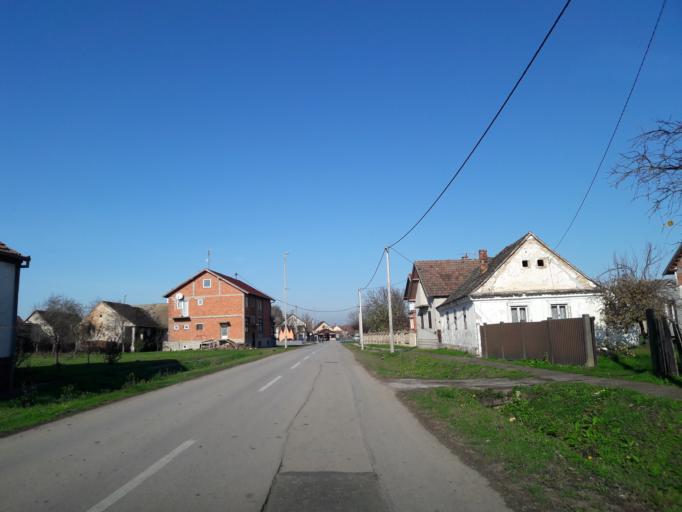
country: HR
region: Vukovarsko-Srijemska
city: Vodinci
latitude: 45.2744
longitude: 18.6107
